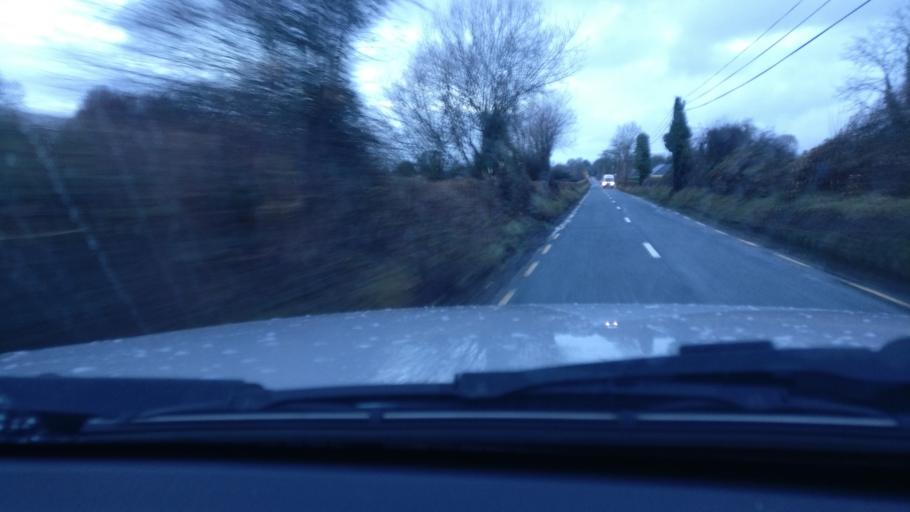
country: IE
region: Connaught
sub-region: County Galway
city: Ballinasloe
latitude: 53.2711
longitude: -8.2473
